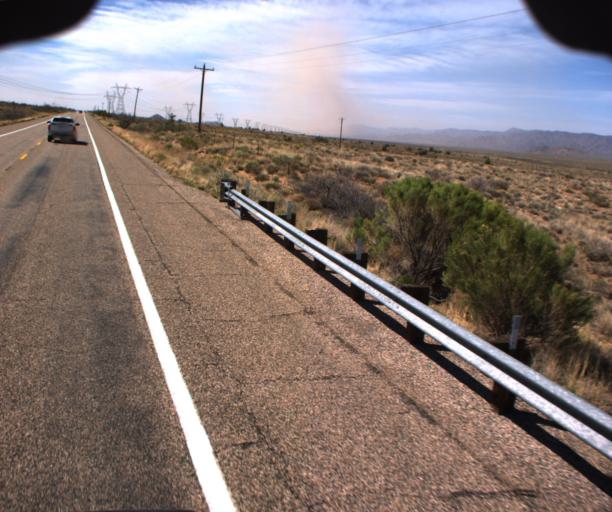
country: US
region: Arizona
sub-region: Mohave County
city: New Kingman-Butler
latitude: 35.3925
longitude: -113.7456
